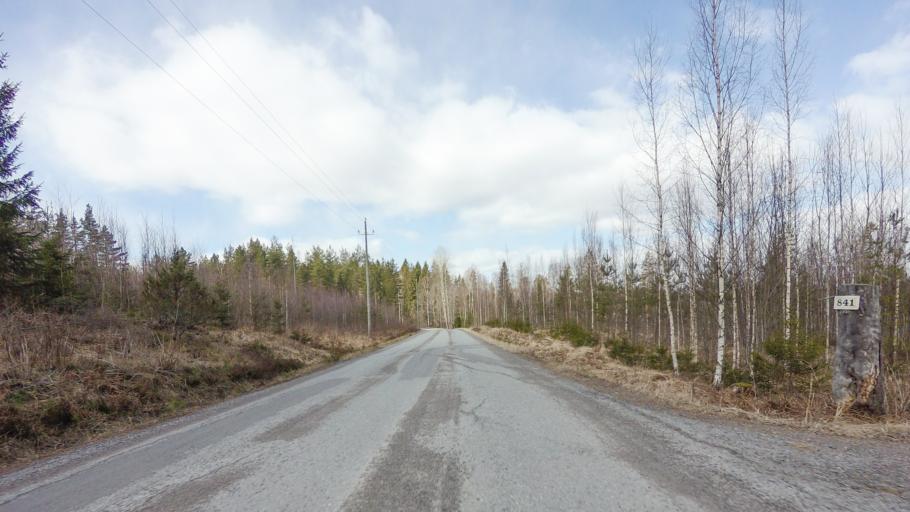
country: FI
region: Varsinais-Suomi
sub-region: Salo
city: Suomusjaervi
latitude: 60.2873
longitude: 23.6502
